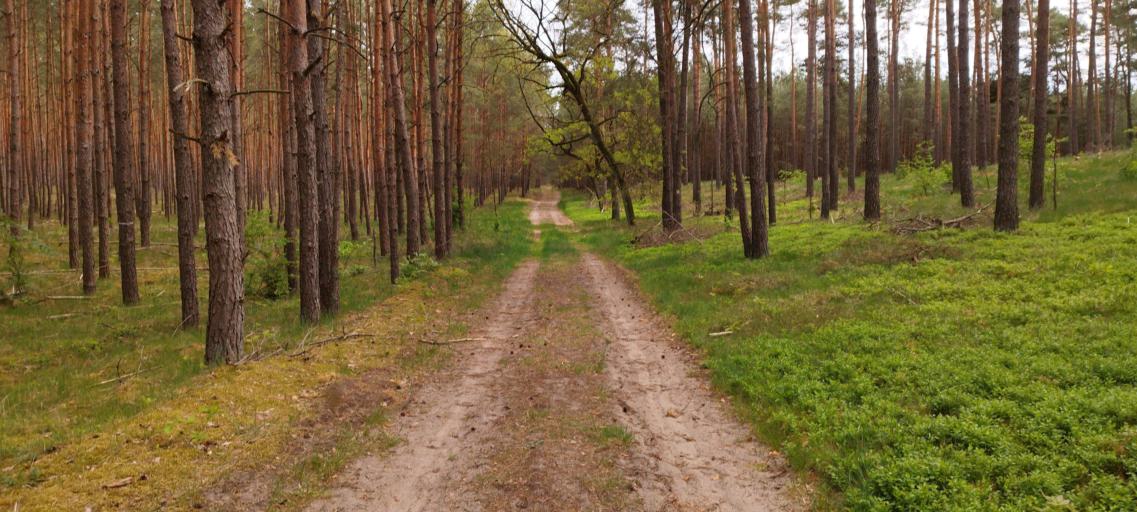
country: DE
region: Brandenburg
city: Spreenhagen
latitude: 52.3846
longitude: 13.9244
